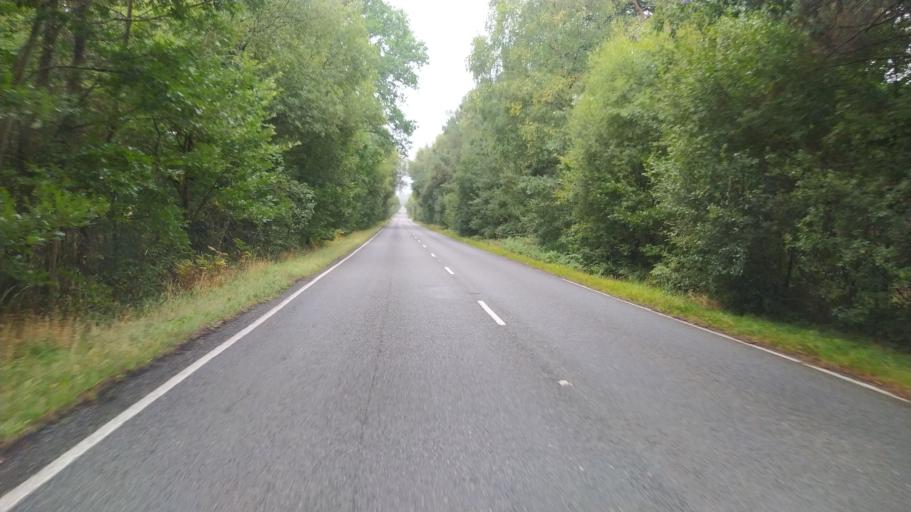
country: GB
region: England
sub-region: Hampshire
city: Sway
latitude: 50.8355
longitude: -1.6457
